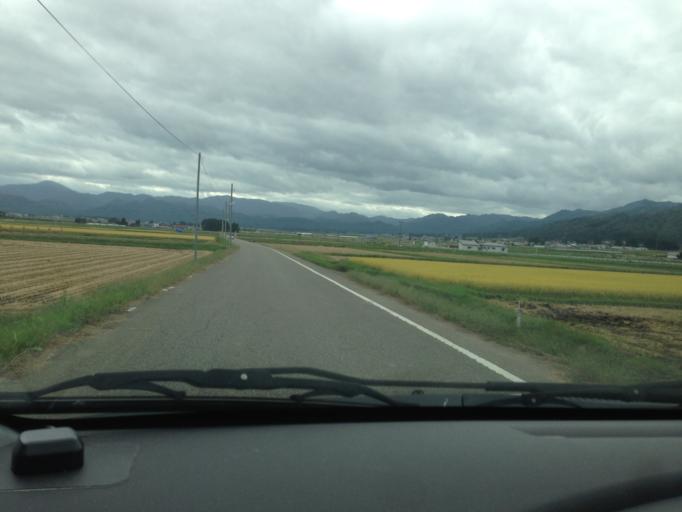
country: JP
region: Fukushima
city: Kitakata
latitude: 37.5052
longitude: 139.8299
